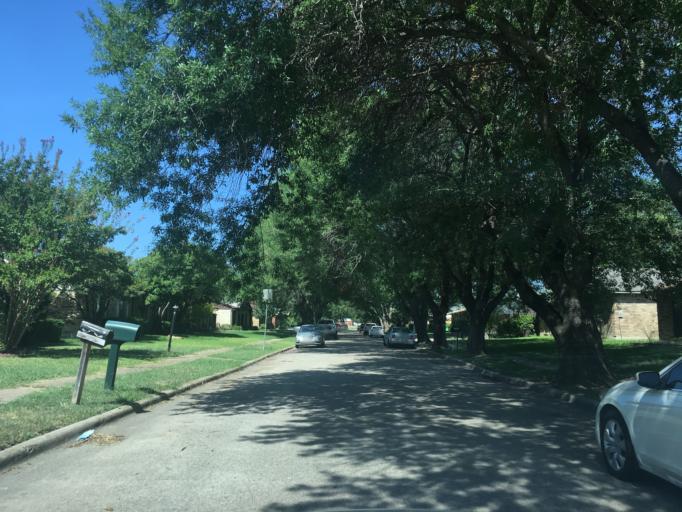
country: US
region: Texas
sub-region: Dallas County
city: Garland
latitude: 32.8548
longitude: -96.6631
